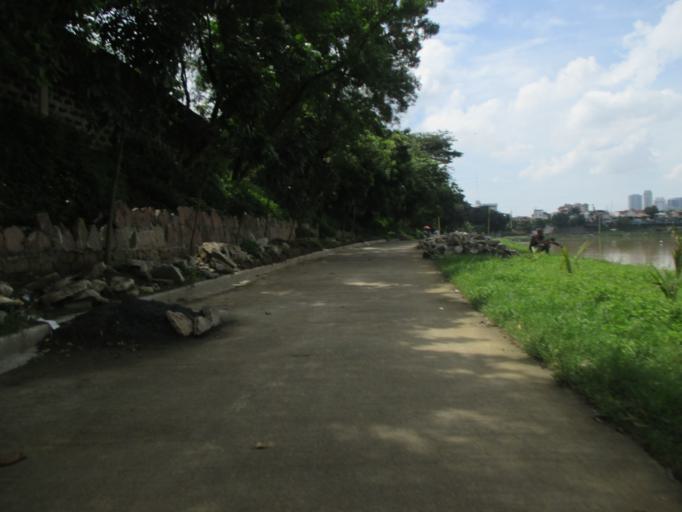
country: PH
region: Metro Manila
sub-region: Marikina
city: Calumpang
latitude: 14.6271
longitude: 121.0943
